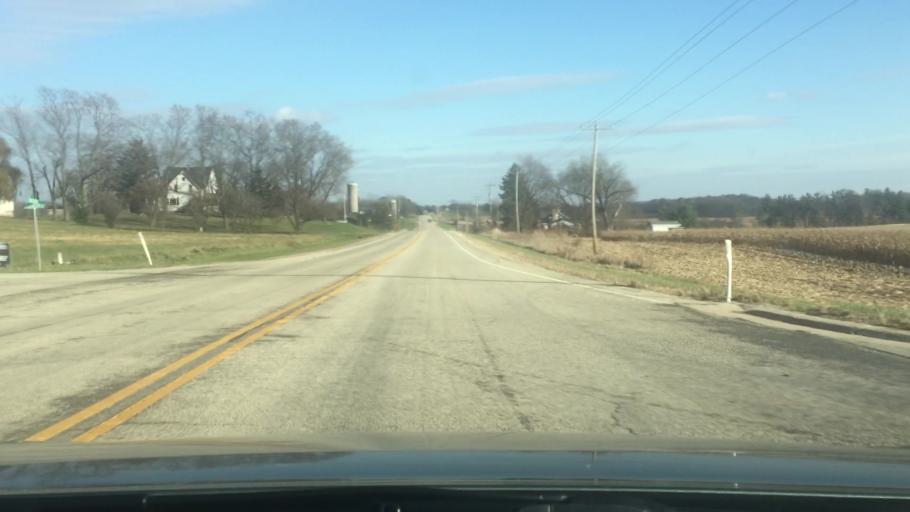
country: US
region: Wisconsin
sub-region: Walworth County
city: Whitewater
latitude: 42.9313
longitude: -88.7144
